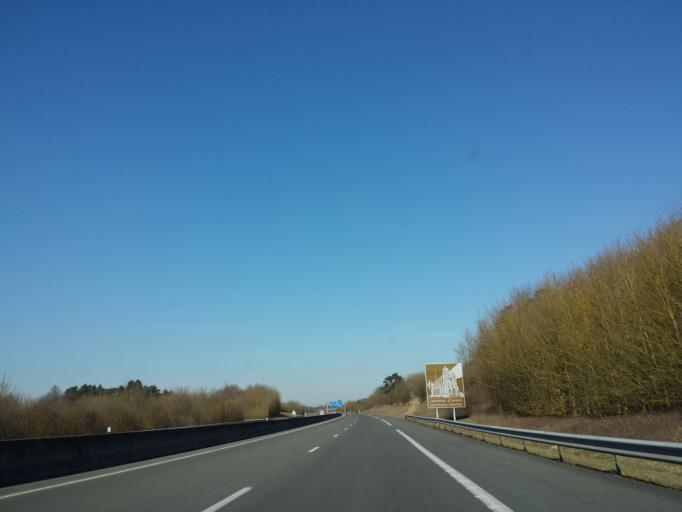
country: FR
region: Picardie
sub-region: Departement de la Somme
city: Saleux
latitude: 49.8403
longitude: 2.2504
